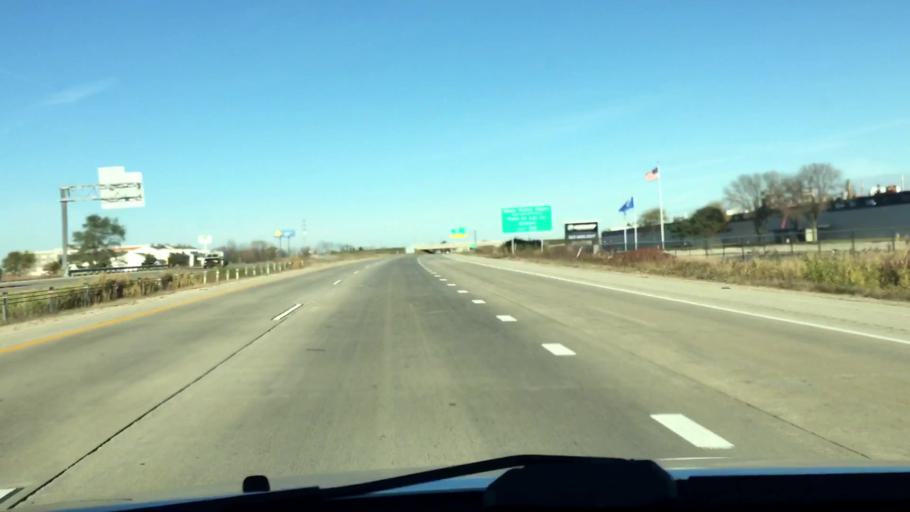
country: US
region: Wisconsin
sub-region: Fond du Lac County
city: Fond du Lac
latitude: 43.7543
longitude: -88.4691
